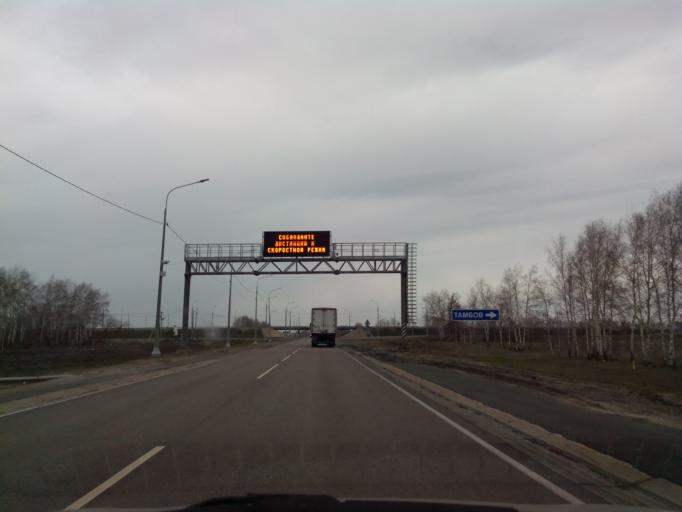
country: RU
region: Tambov
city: Pokrovo-Prigorodnoye
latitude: 52.6573
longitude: 41.3401
